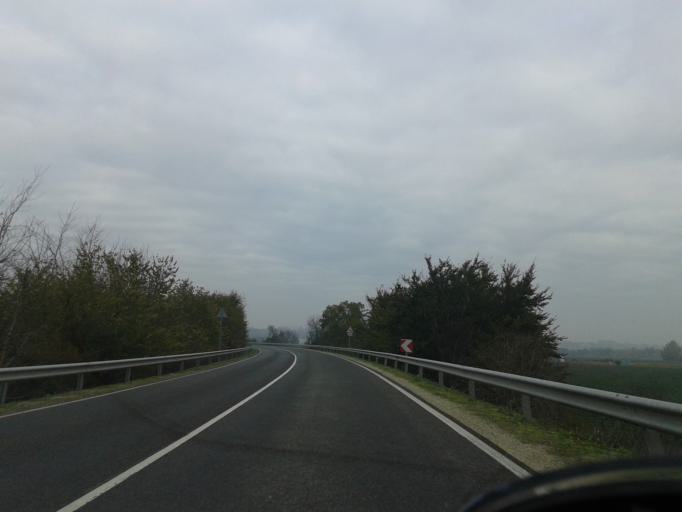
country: HU
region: Fejer
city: Ercsi
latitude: 47.2302
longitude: 18.8932
